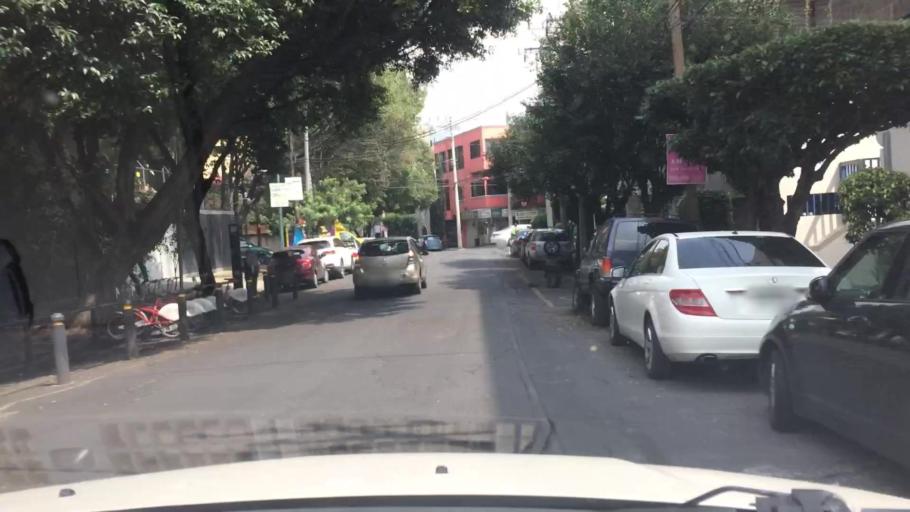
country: MX
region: Mexico City
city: Benito Juarez
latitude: 19.4006
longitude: -99.1638
